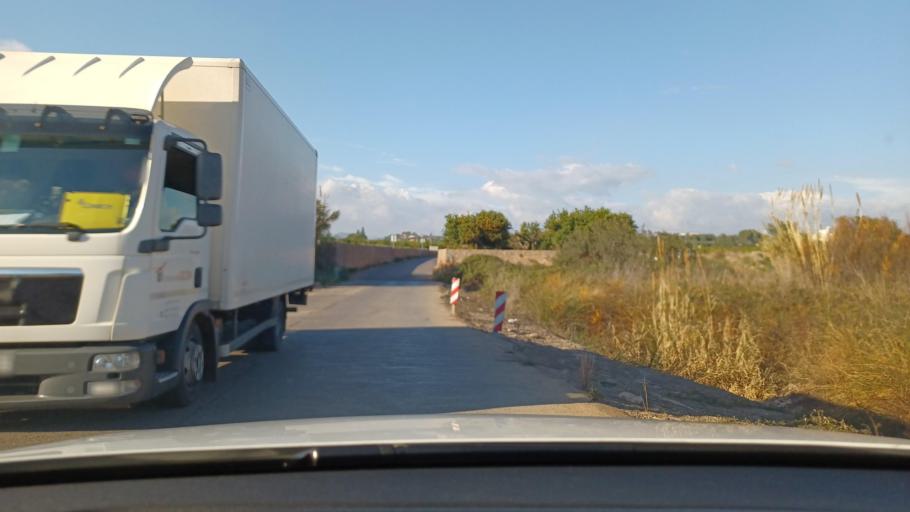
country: ES
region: Valencia
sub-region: Provincia de Castello
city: Betxi
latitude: 39.9468
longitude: -0.2229
